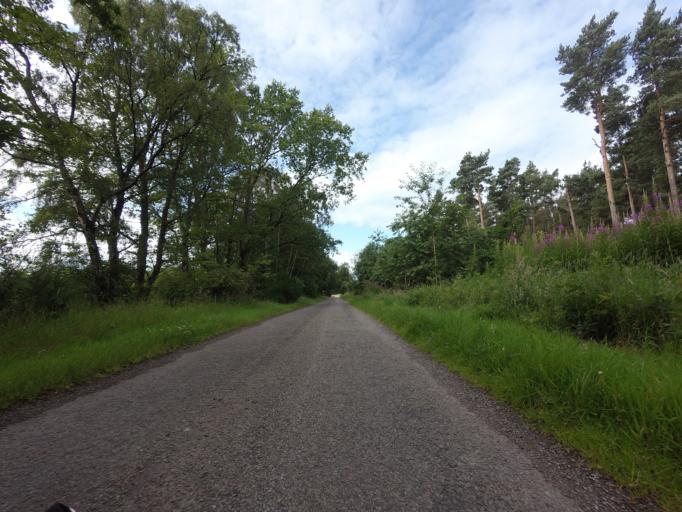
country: GB
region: Scotland
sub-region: Moray
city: Hopeman
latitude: 57.6677
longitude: -3.4205
